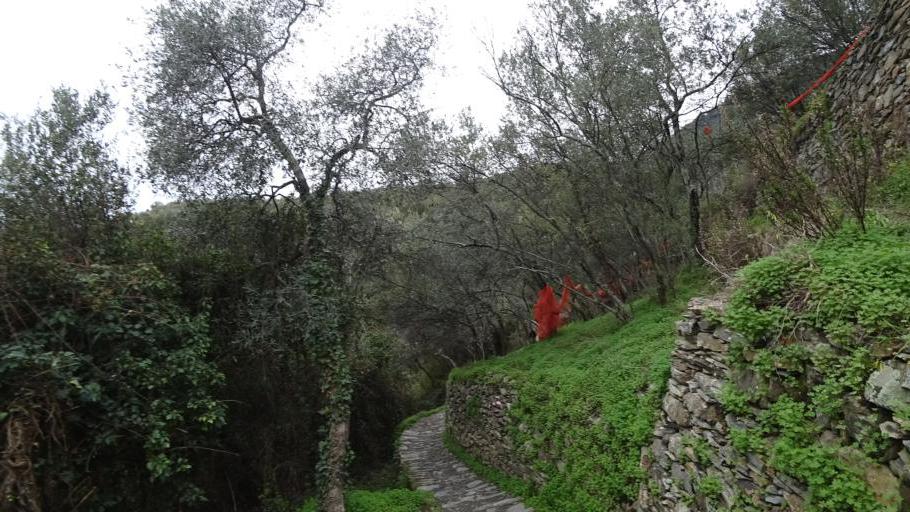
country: IT
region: Liguria
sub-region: Provincia di La Spezia
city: Vernazza
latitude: 44.1243
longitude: 9.7079
